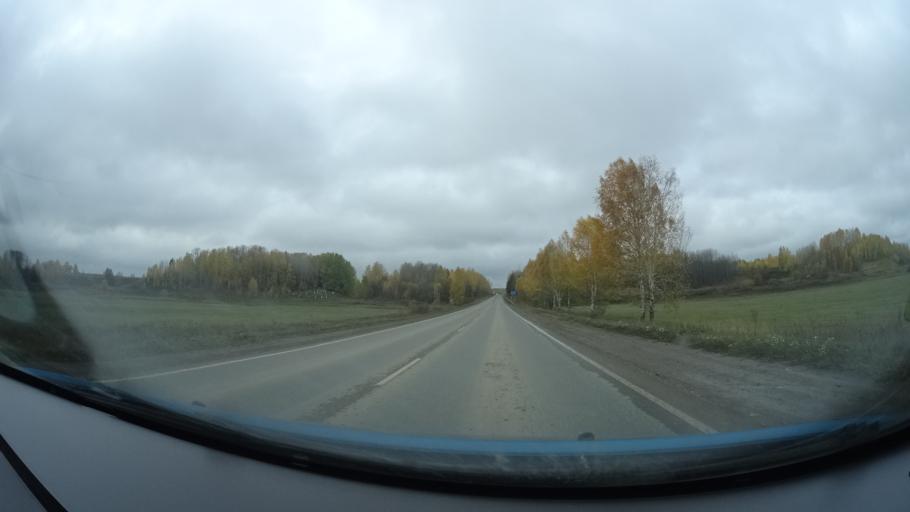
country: RU
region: Perm
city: Osa
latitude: 57.1795
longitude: 55.5514
